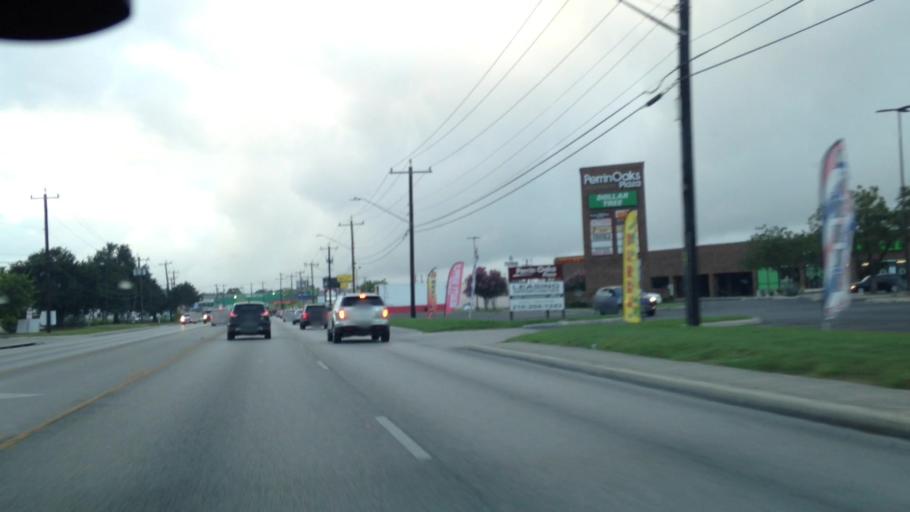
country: US
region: Texas
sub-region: Bexar County
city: Windcrest
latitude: 29.5478
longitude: -98.4093
